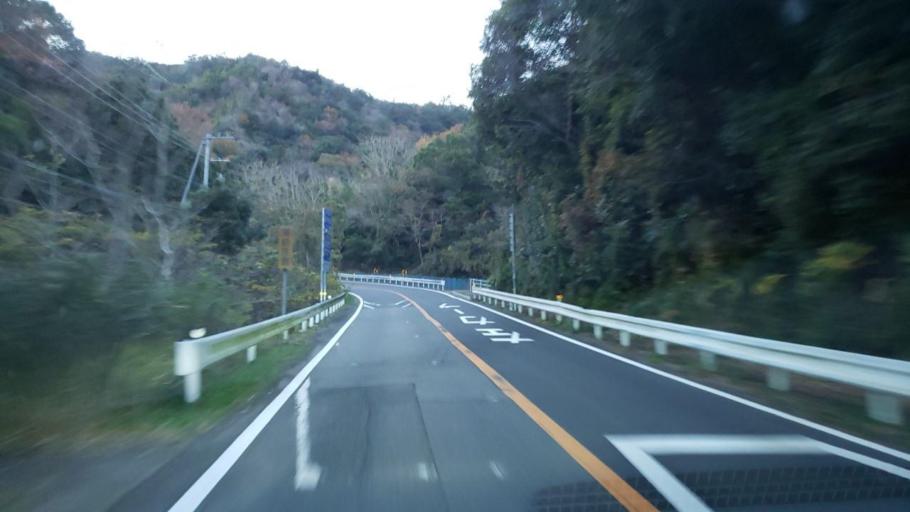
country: JP
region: Hyogo
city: Fukura
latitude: 34.2903
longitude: 134.7141
